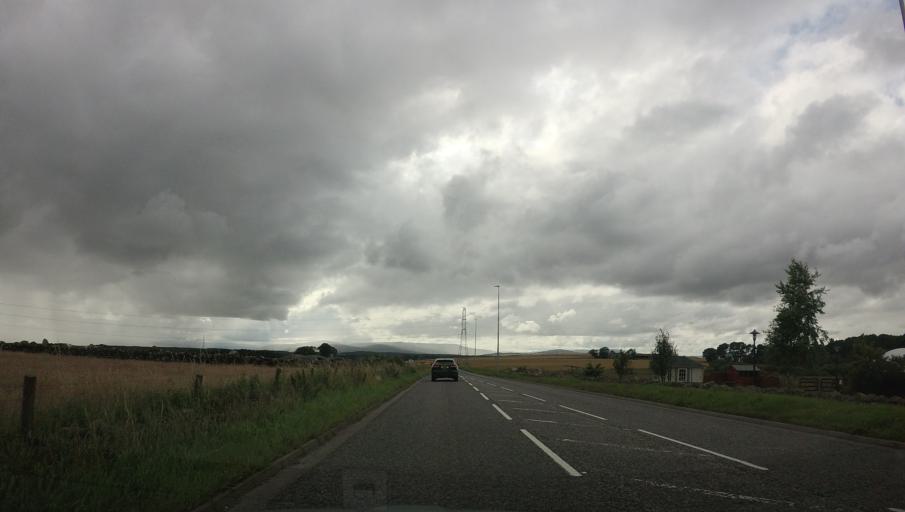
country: GB
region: Scotland
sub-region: Aberdeenshire
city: Westhill
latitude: 57.1435
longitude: -2.3001
